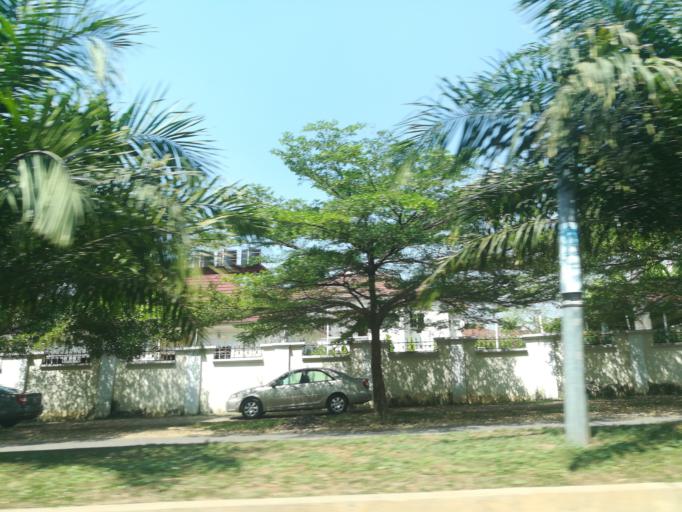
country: NG
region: Abuja Federal Capital Territory
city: Abuja
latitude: 9.0723
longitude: 7.4303
